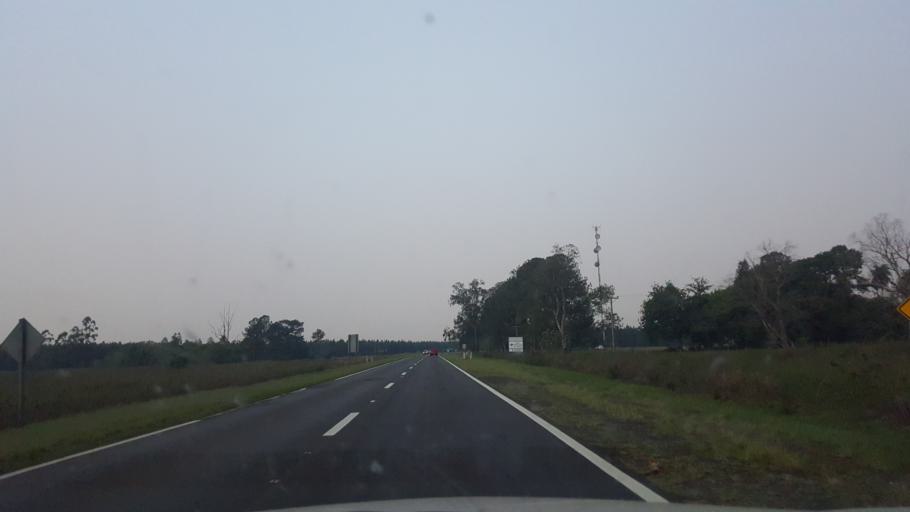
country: PY
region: Misiones
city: Ayolas
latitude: -27.6264
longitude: -56.9187
